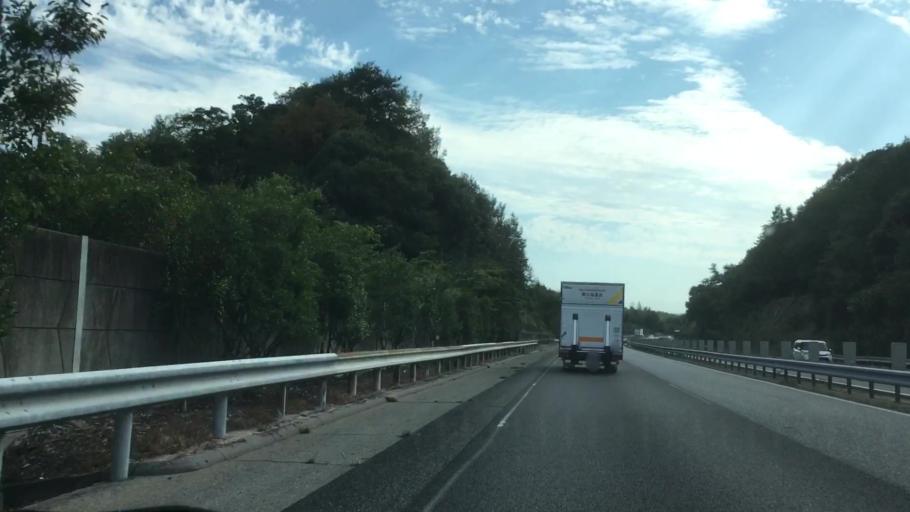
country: JP
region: Hiroshima
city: Ono-hara
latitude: 34.3108
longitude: 132.2803
